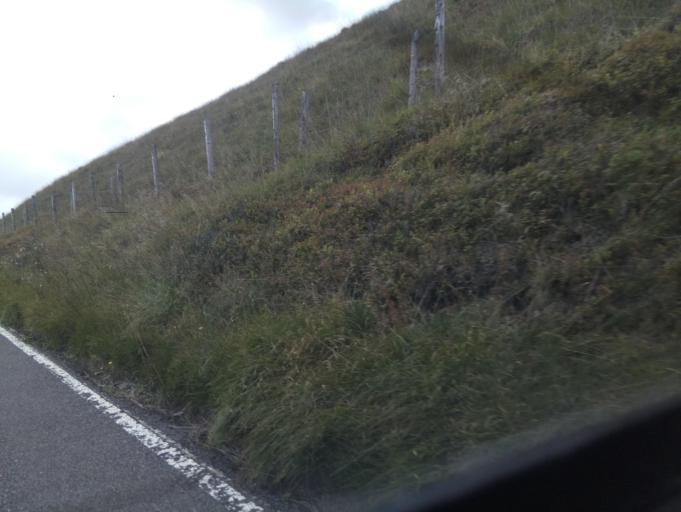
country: GB
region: England
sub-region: Kirklees
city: Meltham
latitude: 53.5089
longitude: -1.8534
